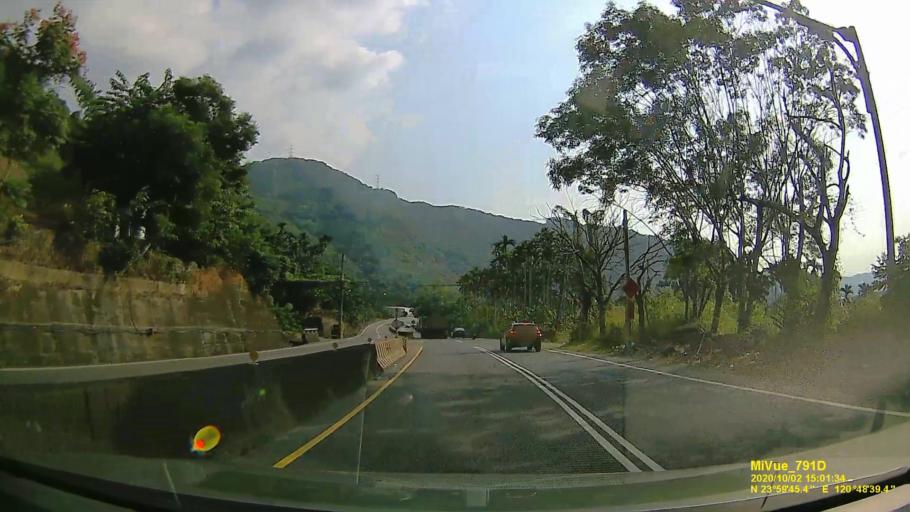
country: TW
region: Taiwan
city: Zhongxing New Village
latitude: 23.9958
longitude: 120.8109
